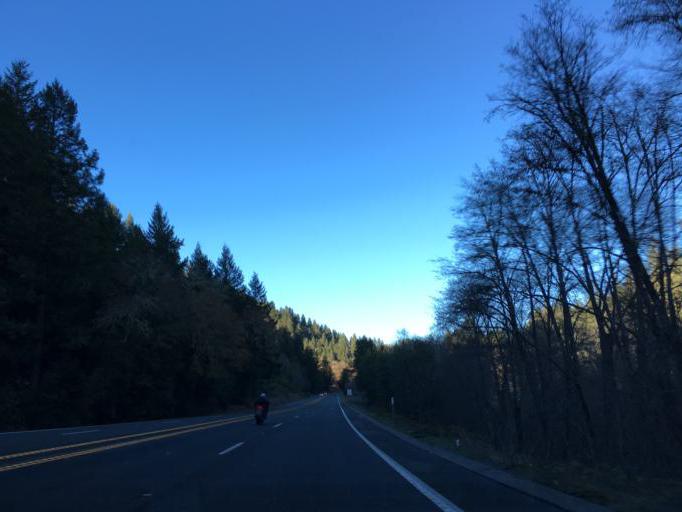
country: US
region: California
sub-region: Mendocino County
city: Laytonville
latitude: 39.5895
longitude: -123.4516
